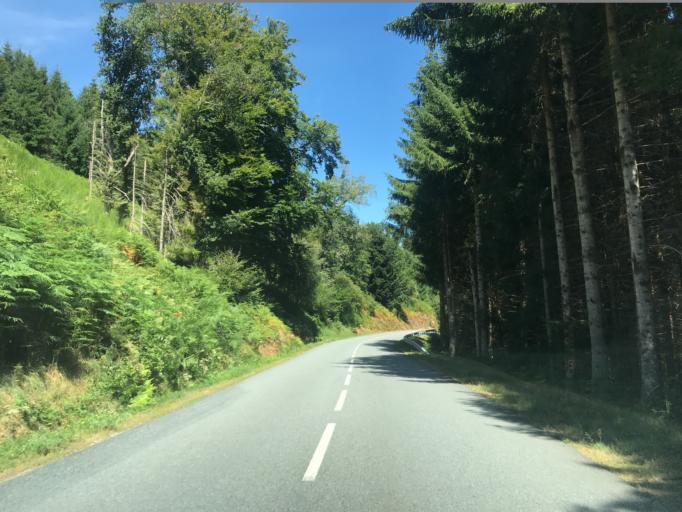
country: FR
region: Limousin
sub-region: Departement de la Creuse
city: Felletin
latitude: 45.7810
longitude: 2.1394
